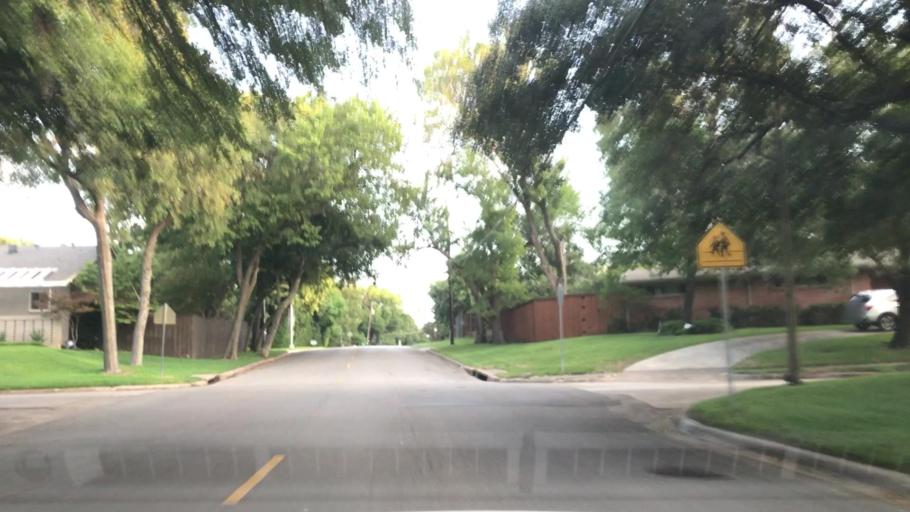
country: US
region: Texas
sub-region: Dallas County
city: University Park
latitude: 32.9028
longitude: -96.7805
